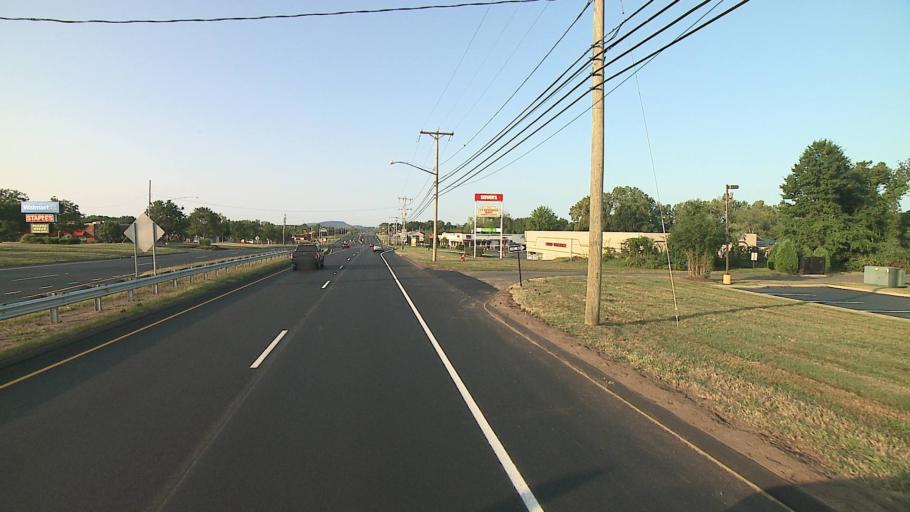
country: US
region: Connecticut
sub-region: Hartford County
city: Newington
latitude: 41.6643
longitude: -72.7210
